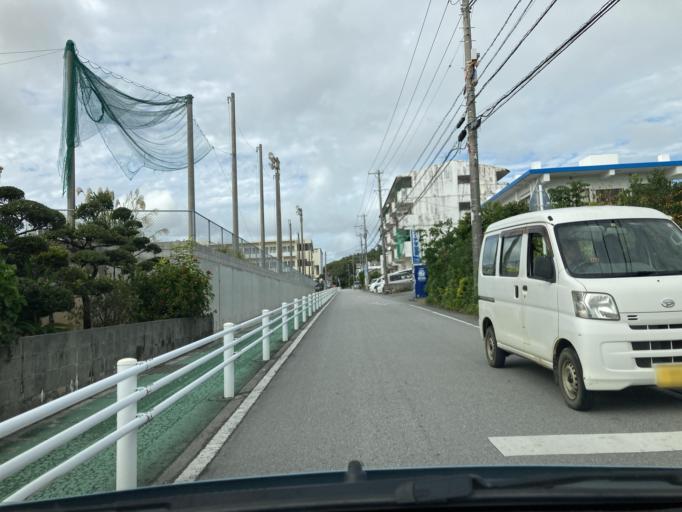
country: JP
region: Okinawa
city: Tomigusuku
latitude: 26.1782
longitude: 127.7467
